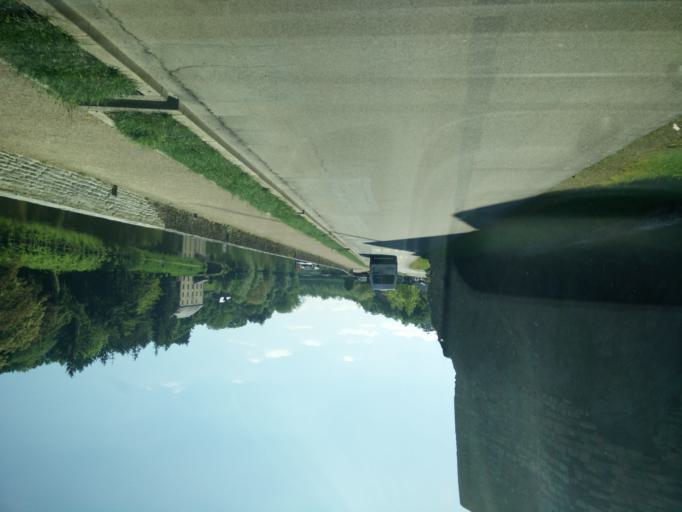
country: FR
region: Brittany
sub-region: Departement du Morbihan
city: Josselin
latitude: 47.9518
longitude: -2.5471
